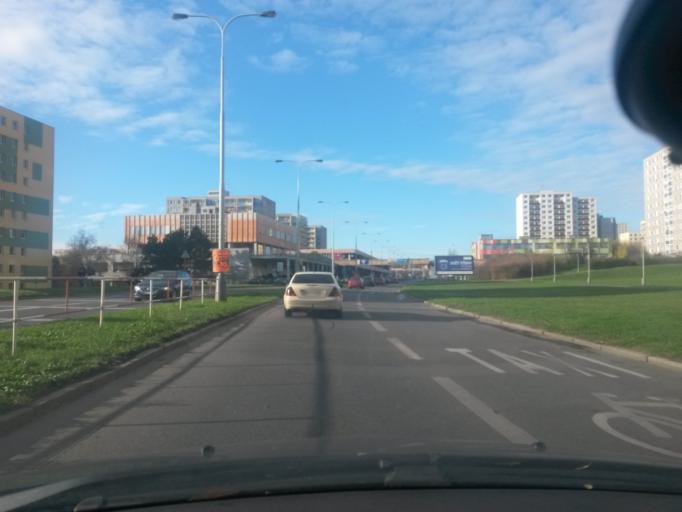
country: CZ
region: Central Bohemia
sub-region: Okres Praha-Zapad
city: Pruhonice
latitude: 50.0260
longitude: 14.5205
